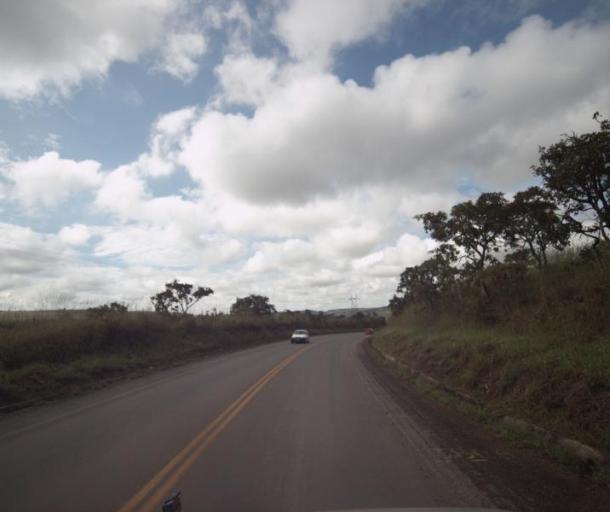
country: BR
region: Goias
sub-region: Pirenopolis
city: Pirenopolis
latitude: -15.8406
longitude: -48.7711
